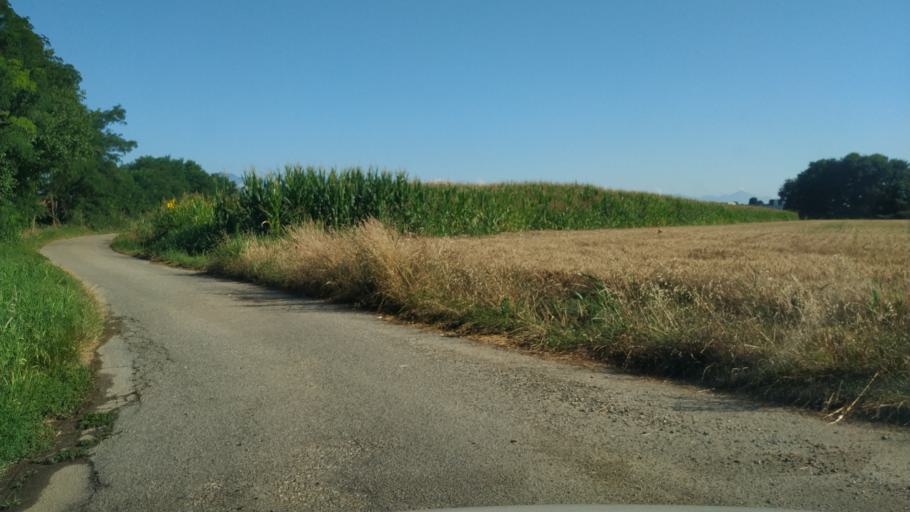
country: IT
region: Piedmont
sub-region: Provincia di Vercelli
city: Alice Castello
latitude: 45.3571
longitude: 8.0790
